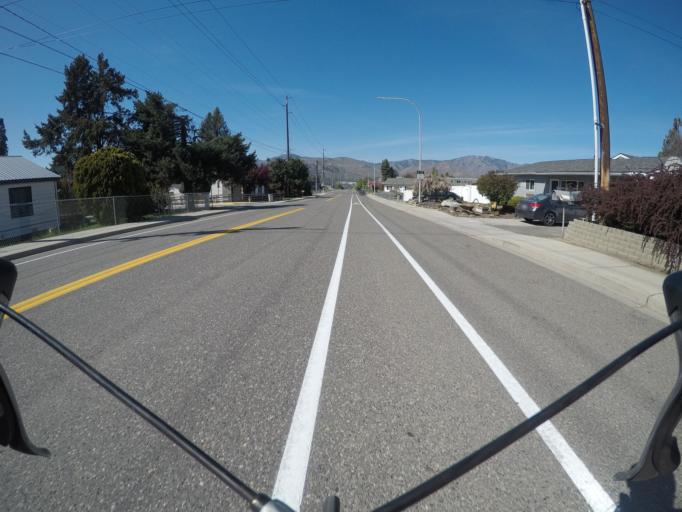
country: US
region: Washington
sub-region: Douglas County
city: East Wenatchee Bench
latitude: 47.4218
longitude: -120.2859
